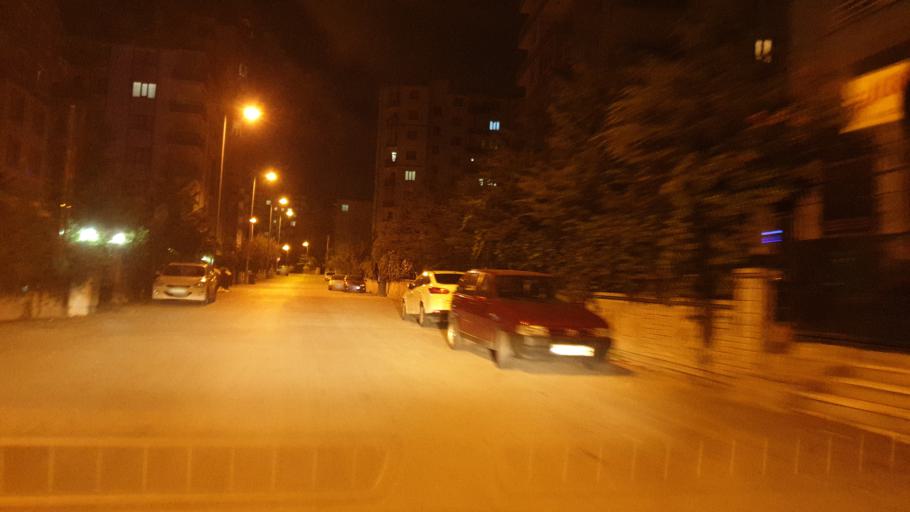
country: TR
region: Kayseri
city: Talas
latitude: 38.6962
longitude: 35.5420
